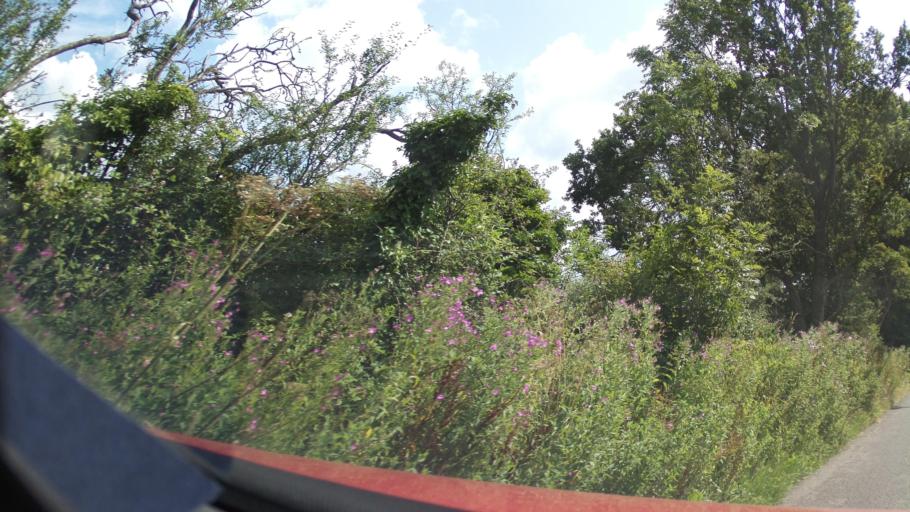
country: GB
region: England
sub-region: Wiltshire
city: Minety
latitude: 51.6019
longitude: -1.9457
